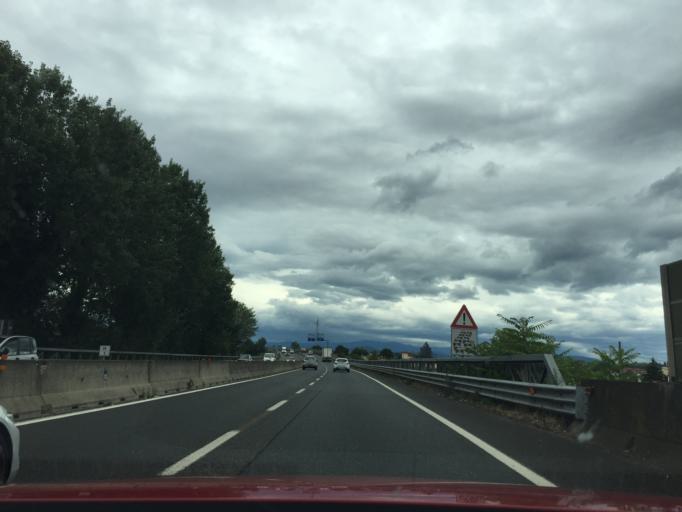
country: IT
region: Tuscany
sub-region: Province of Florence
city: Mantignano-Ugnano
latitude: 43.7703
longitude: 11.1776
